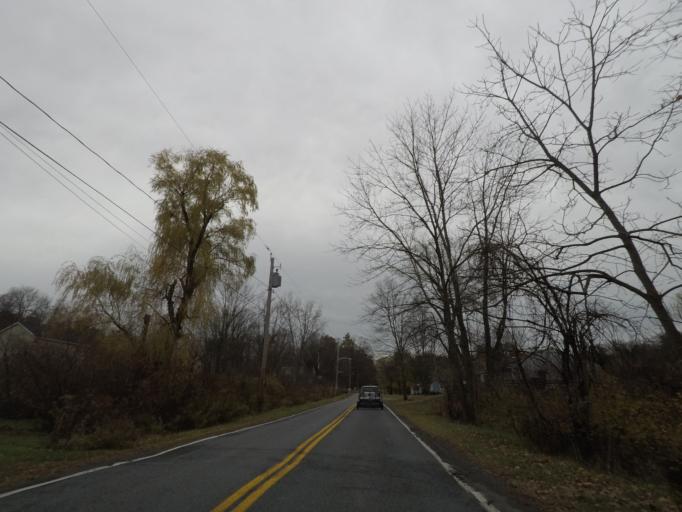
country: US
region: New York
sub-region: Rensselaer County
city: Troy
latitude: 42.7308
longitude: -73.6561
